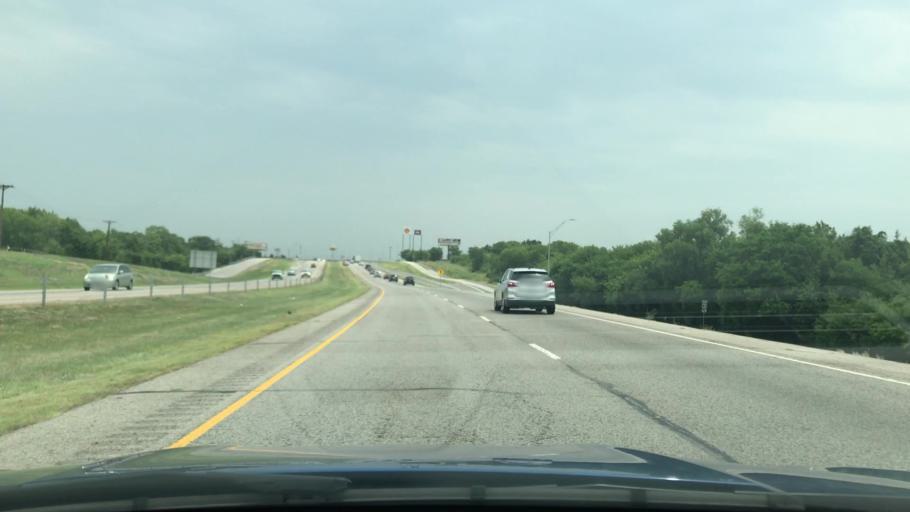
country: US
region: Texas
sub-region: Kaufman County
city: Forney
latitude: 32.7588
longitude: -96.4760
